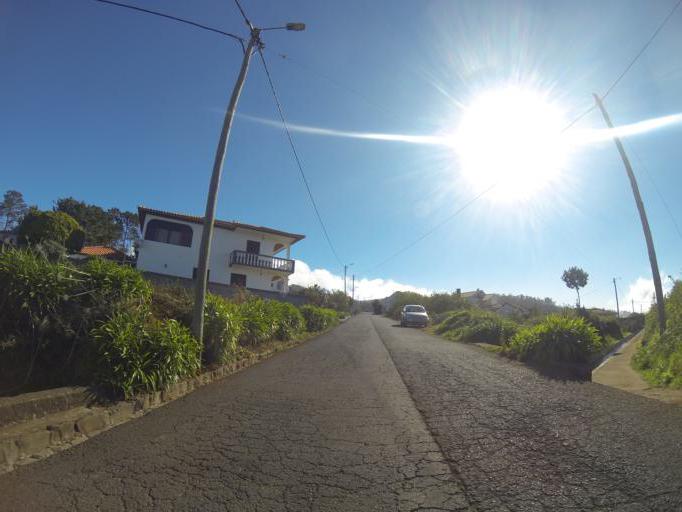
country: PT
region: Madeira
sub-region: Calheta
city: Estreito da Calheta
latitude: 32.7579
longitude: -17.1979
